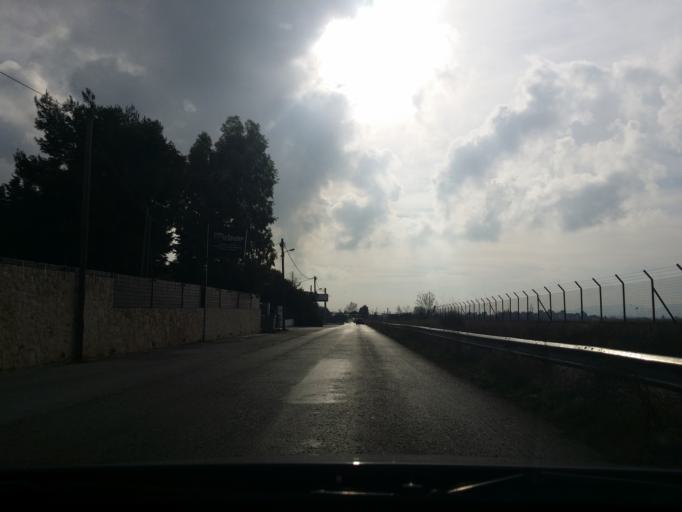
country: GR
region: Attica
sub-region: Nomarchia Anatolikis Attikis
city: Varybobi
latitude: 38.1081
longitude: 23.7898
